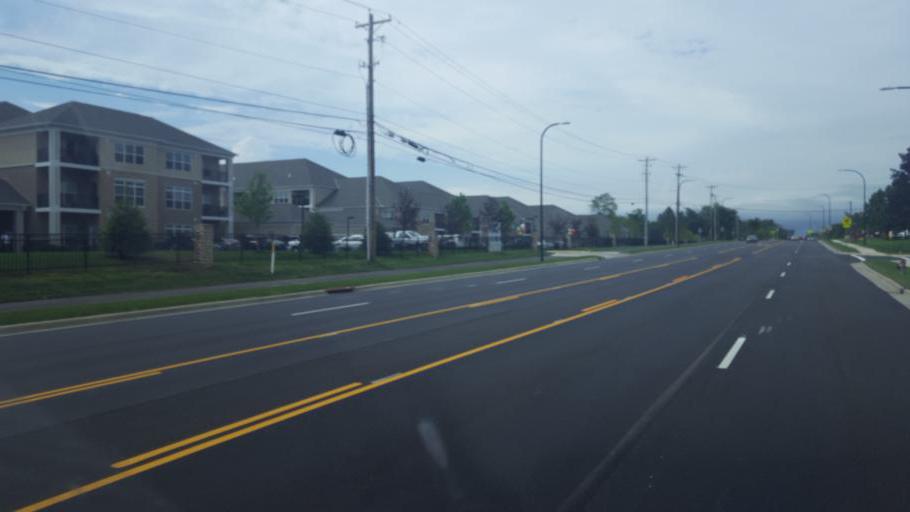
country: US
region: Ohio
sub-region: Franklin County
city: Gahanna
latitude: 40.0292
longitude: -82.8657
